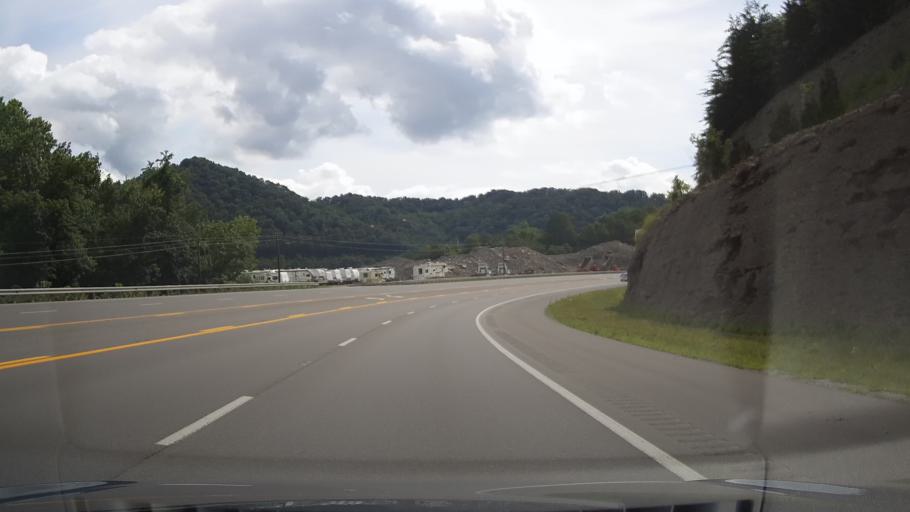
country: US
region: Kentucky
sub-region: Pike County
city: Coal Run Village
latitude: 37.5377
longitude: -82.5952
